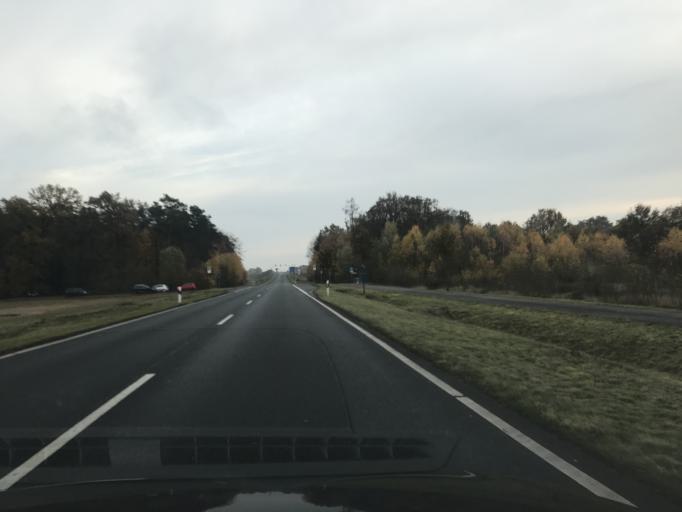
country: DE
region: North Rhine-Westphalia
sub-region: Regierungsbezirk Munster
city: Ladbergen
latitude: 52.1185
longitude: 7.6975
